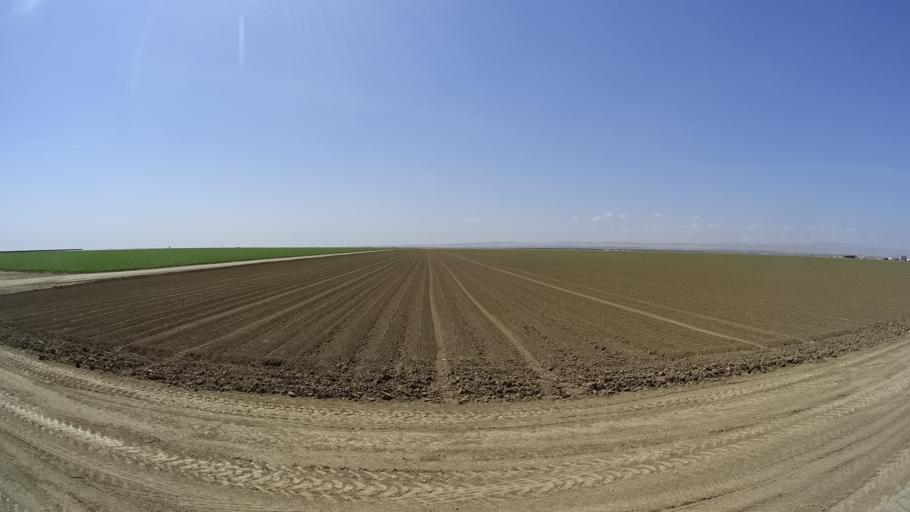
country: US
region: California
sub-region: Kings County
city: Kettleman City
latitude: 36.1377
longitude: -119.9773
